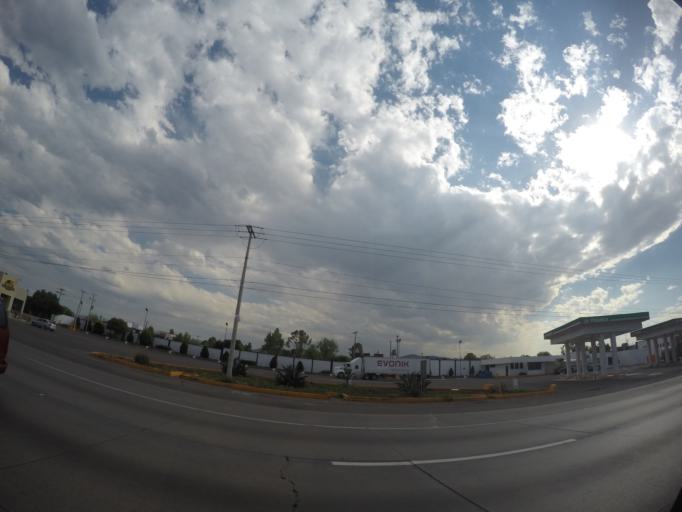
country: MX
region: Queretaro
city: Pedro Escobedo
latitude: 20.5046
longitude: -100.1427
